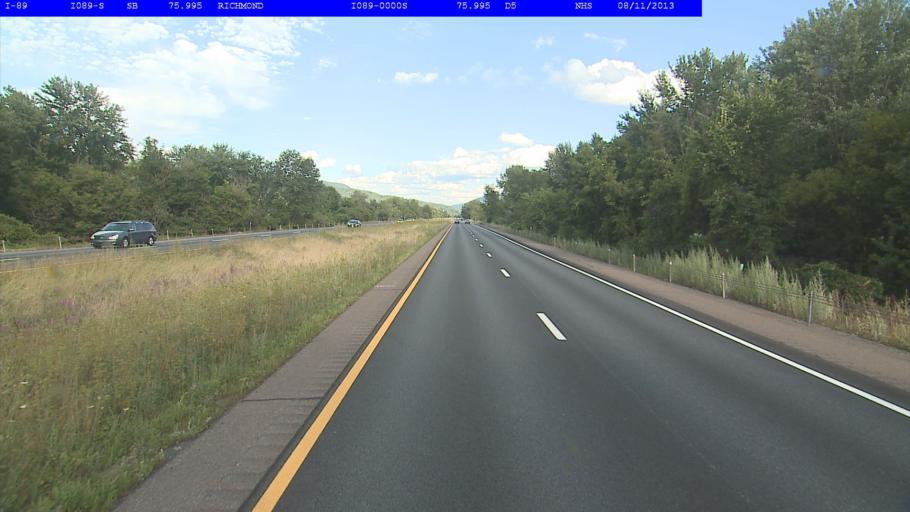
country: US
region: Vermont
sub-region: Chittenden County
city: Williston
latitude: 44.3992
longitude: -72.9803
